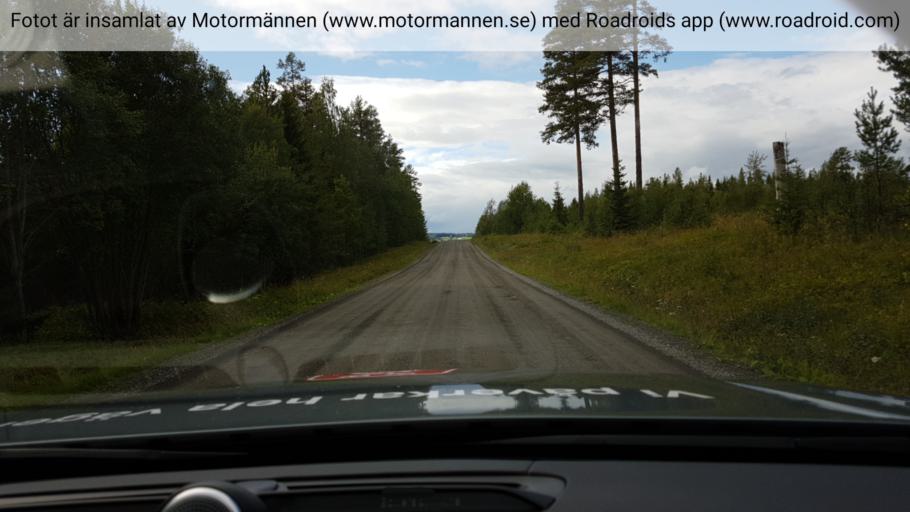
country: SE
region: Jaemtland
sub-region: OEstersunds Kommun
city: Lit
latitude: 63.6781
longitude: 14.8099
